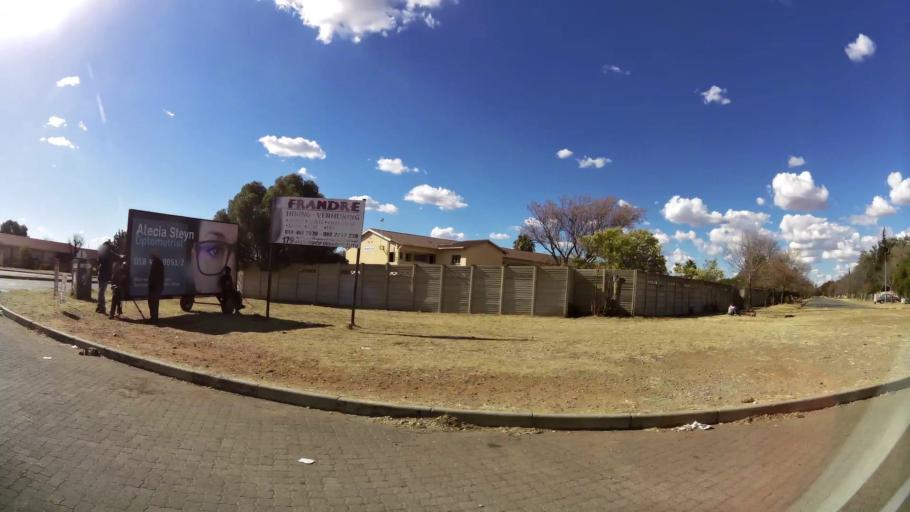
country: ZA
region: North-West
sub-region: Dr Kenneth Kaunda District Municipality
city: Klerksdorp
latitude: -26.8574
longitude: 26.6442
